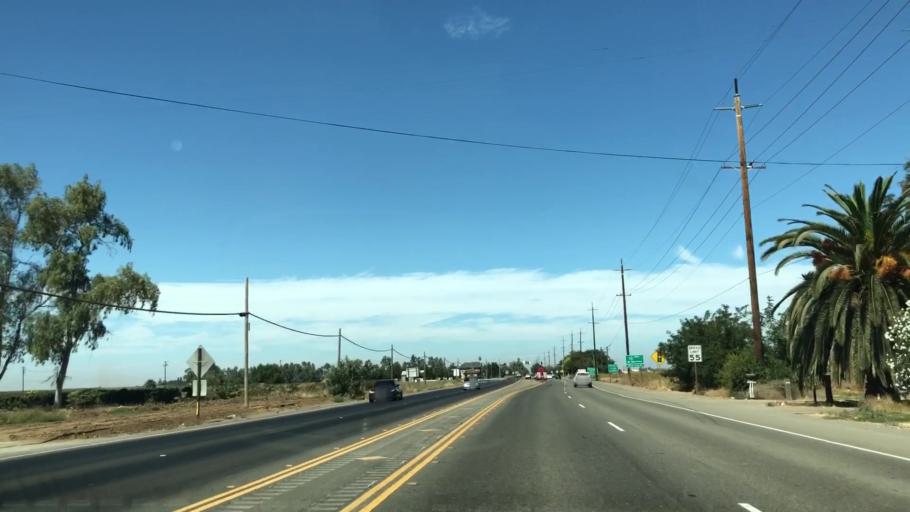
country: US
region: California
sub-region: Contra Costa County
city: Byron
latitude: 37.8929
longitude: -121.6413
